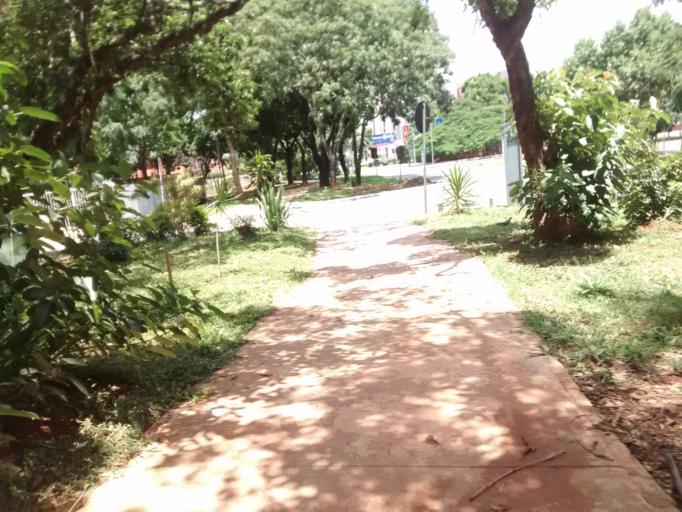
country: BR
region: Federal District
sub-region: Brasilia
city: Brasilia
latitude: -15.8154
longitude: -47.9149
